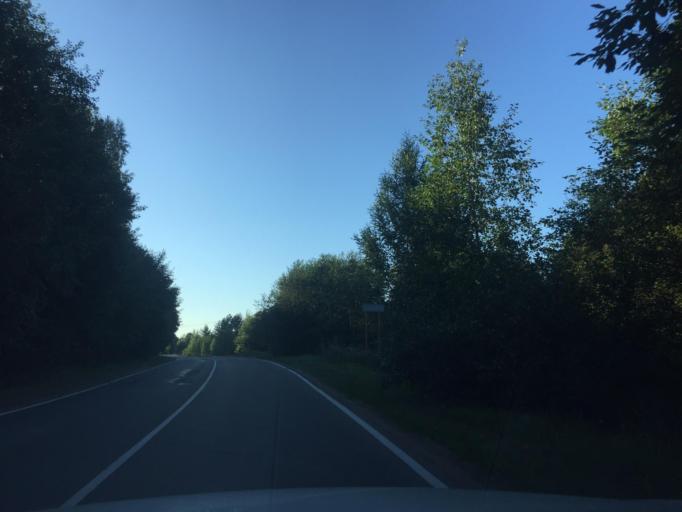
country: RU
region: Leningrad
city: Siverskiy
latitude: 59.3407
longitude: 30.0231
